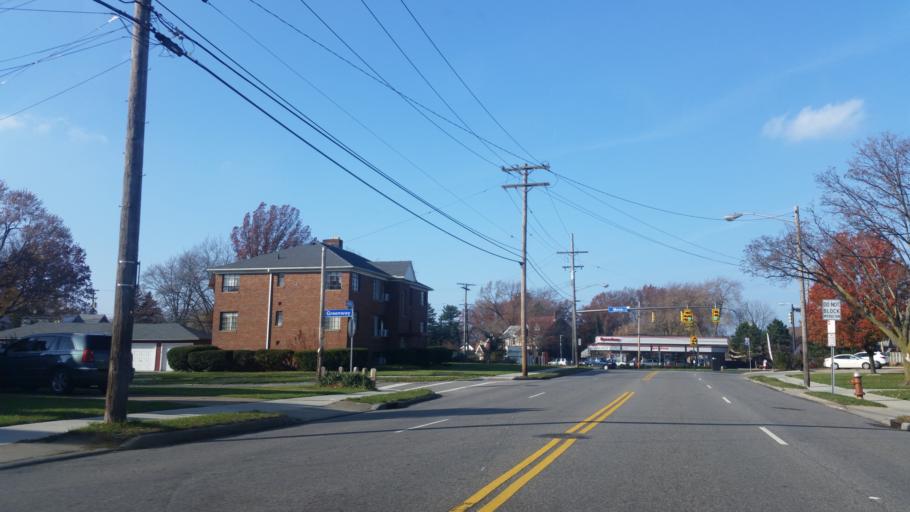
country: US
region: Ohio
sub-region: Cuyahoga County
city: Lakewood
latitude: 41.4580
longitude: -81.8042
